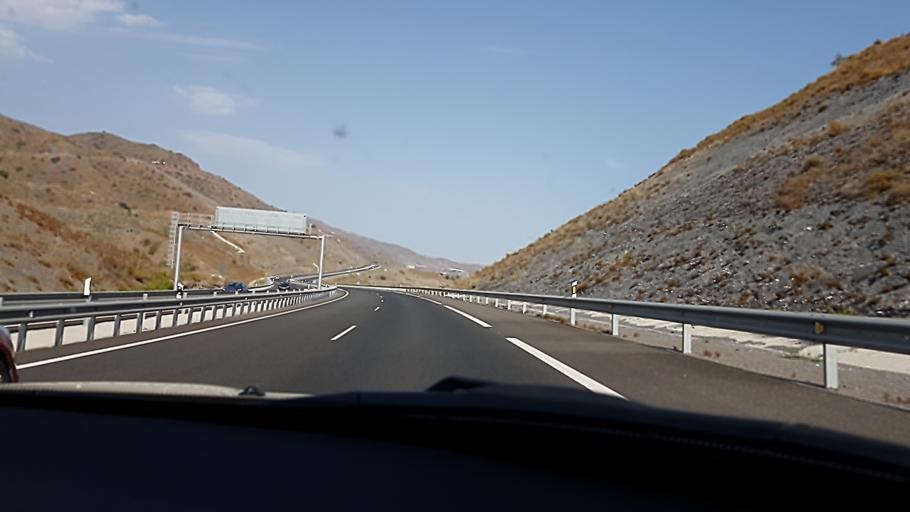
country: ES
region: Andalusia
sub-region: Provincia de Granada
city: Polopos
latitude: 36.7511
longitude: -3.2825
